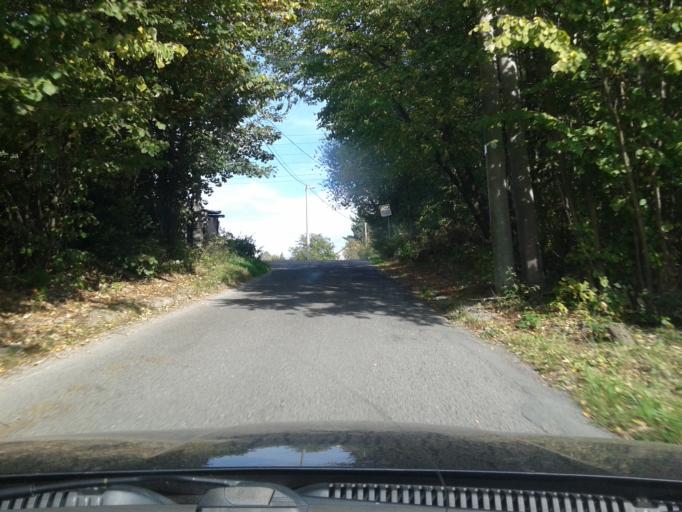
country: CZ
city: Doubrava
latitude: 49.8590
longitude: 18.4572
